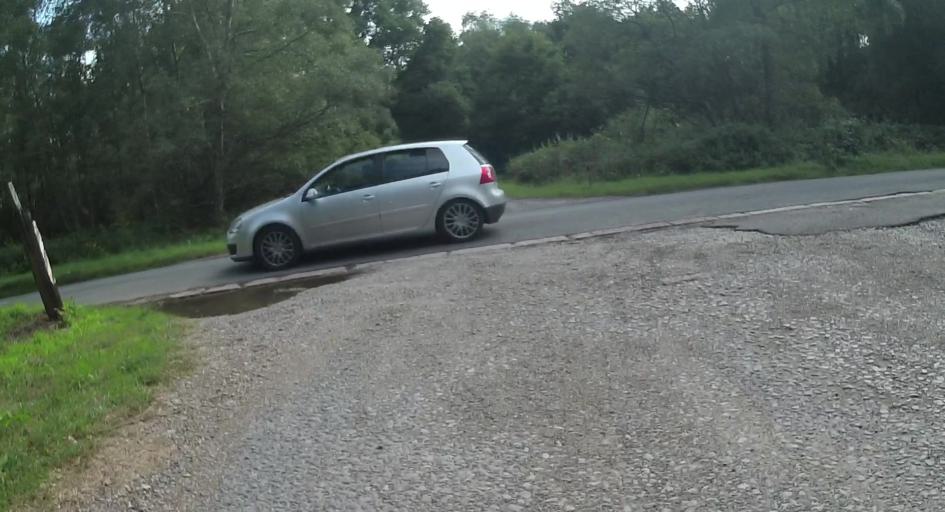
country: GB
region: England
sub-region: West Berkshire
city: Thatcham
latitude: 51.3771
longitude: -1.2422
